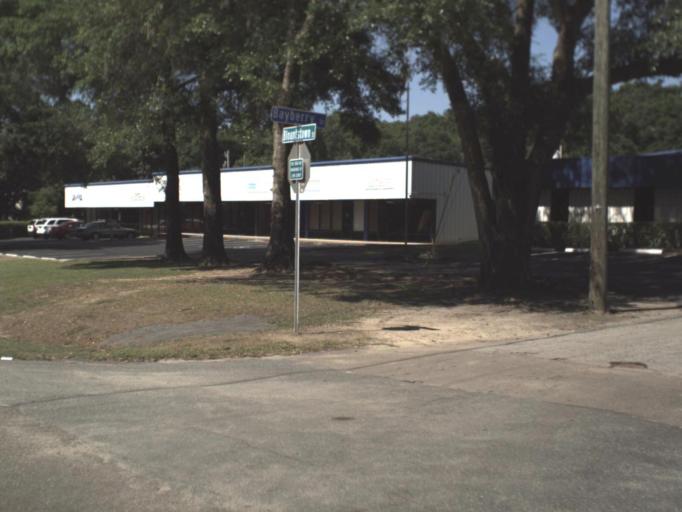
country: US
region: Florida
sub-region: Leon County
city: Tallahassee
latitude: 30.4452
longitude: -84.3470
